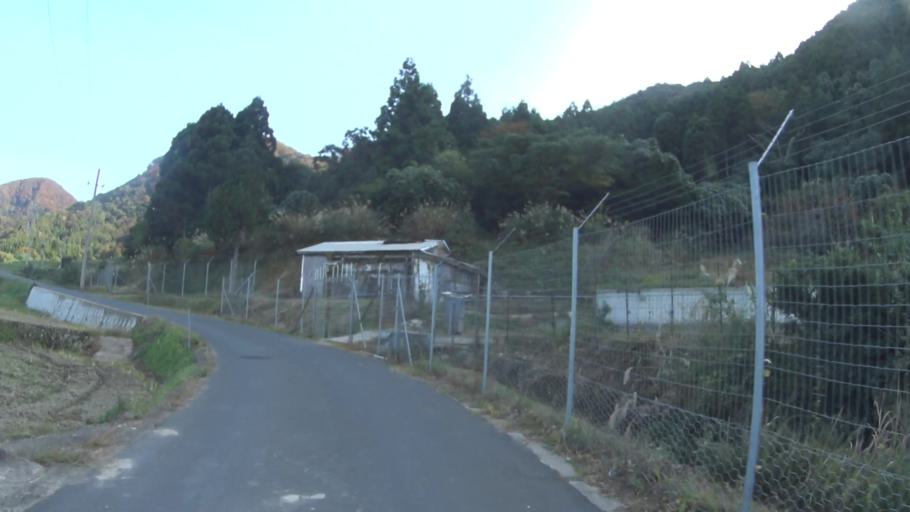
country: JP
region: Kyoto
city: Miyazu
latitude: 35.7625
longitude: 135.2005
